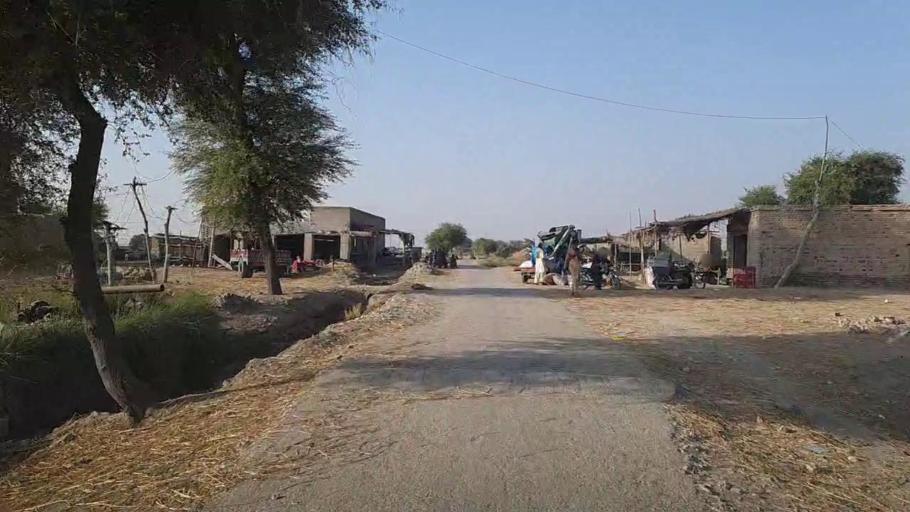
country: PK
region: Sindh
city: Kashmor
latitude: 28.4132
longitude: 69.4113
